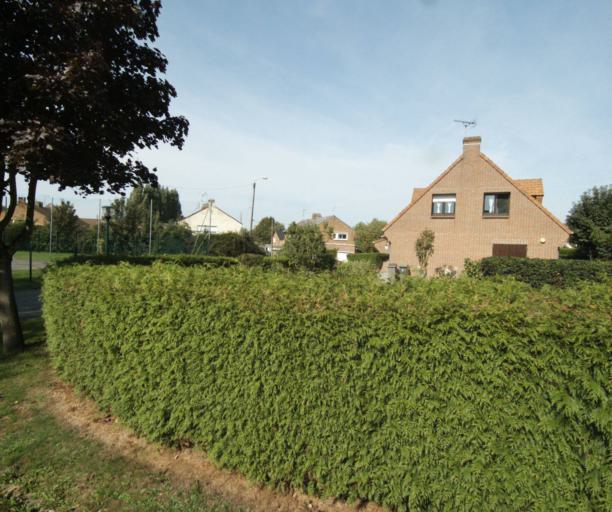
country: FR
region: Nord-Pas-de-Calais
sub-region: Departement du Nord
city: Capinghem
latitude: 50.6446
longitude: 2.9630
